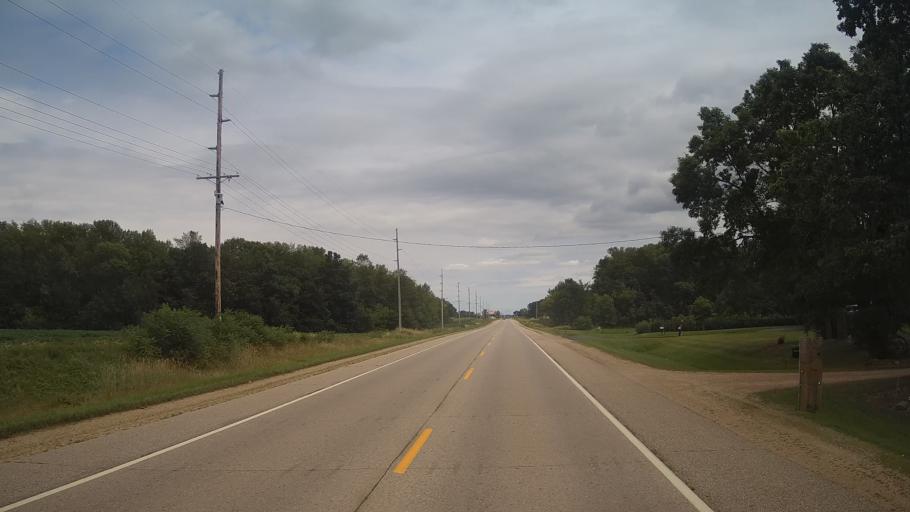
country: US
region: Wisconsin
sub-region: Green Lake County
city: Berlin
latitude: 44.0410
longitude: -88.9998
